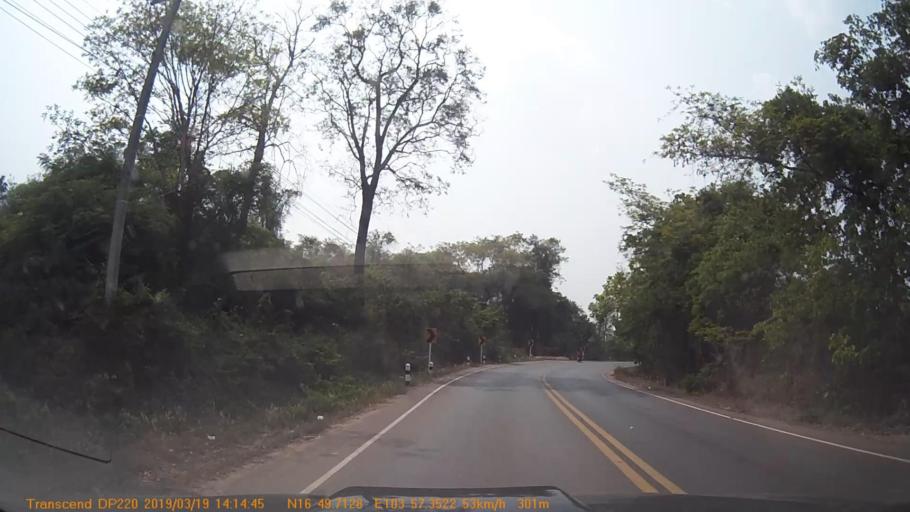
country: TH
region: Kalasin
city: Na Khu
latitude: 16.8287
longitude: 103.9555
